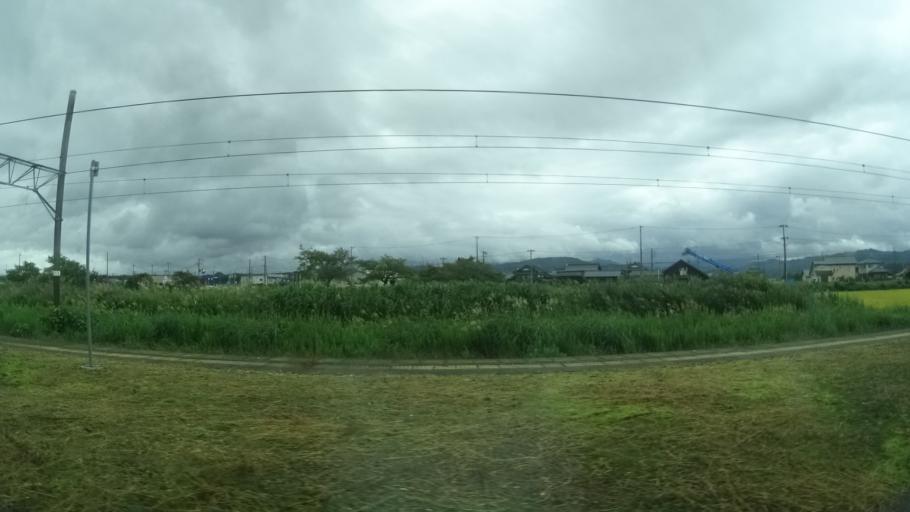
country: JP
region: Niigata
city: Murakami
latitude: 38.1837
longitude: 139.4597
